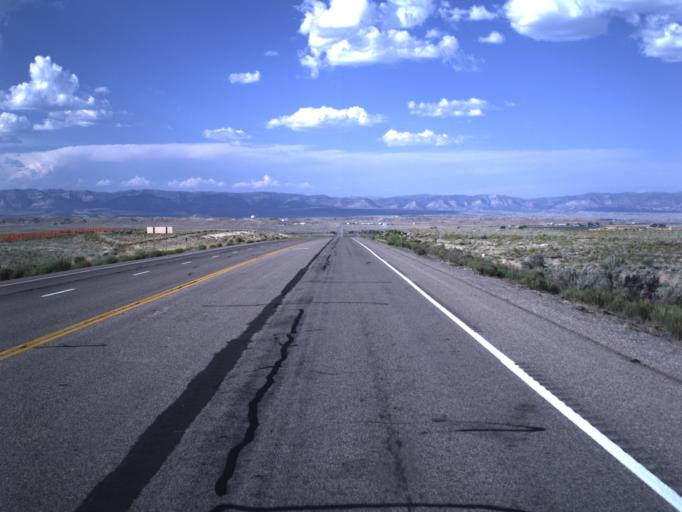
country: US
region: Utah
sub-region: Carbon County
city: Price
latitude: 39.4947
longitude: -110.8445
